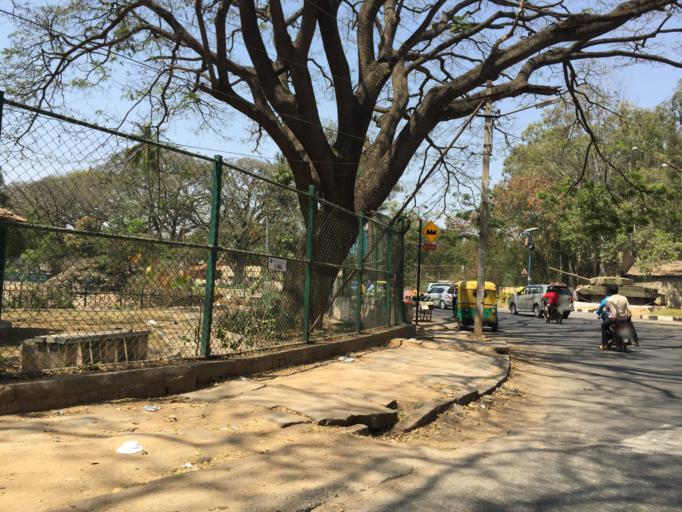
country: IN
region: Karnataka
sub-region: Bangalore Urban
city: Bangalore
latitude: 12.9872
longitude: 77.6225
